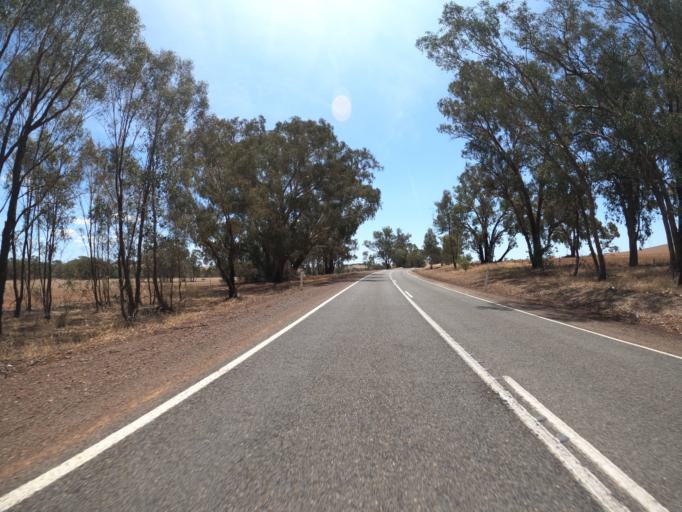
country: AU
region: Victoria
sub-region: Benalla
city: Benalla
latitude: -36.3434
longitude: 145.9593
